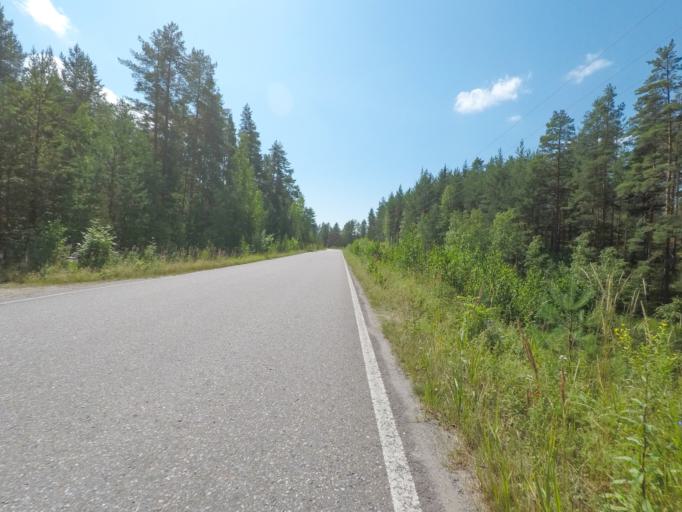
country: FI
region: Southern Savonia
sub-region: Mikkeli
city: Puumala
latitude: 61.5049
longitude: 28.1675
